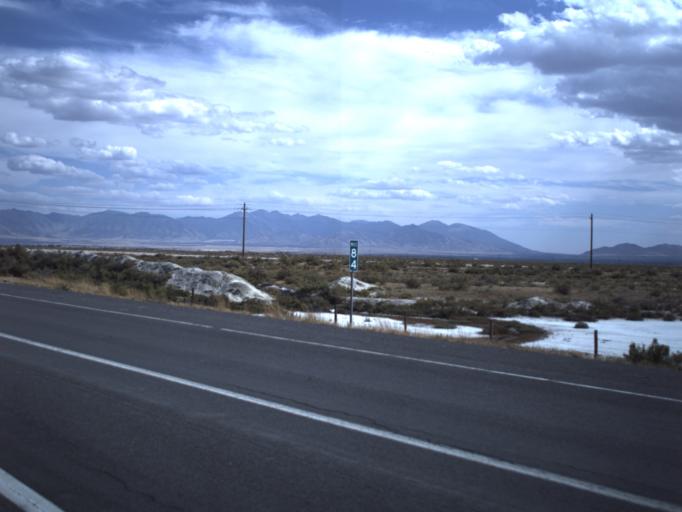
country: US
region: Utah
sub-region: Tooele County
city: Grantsville
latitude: 40.7058
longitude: -112.5191
